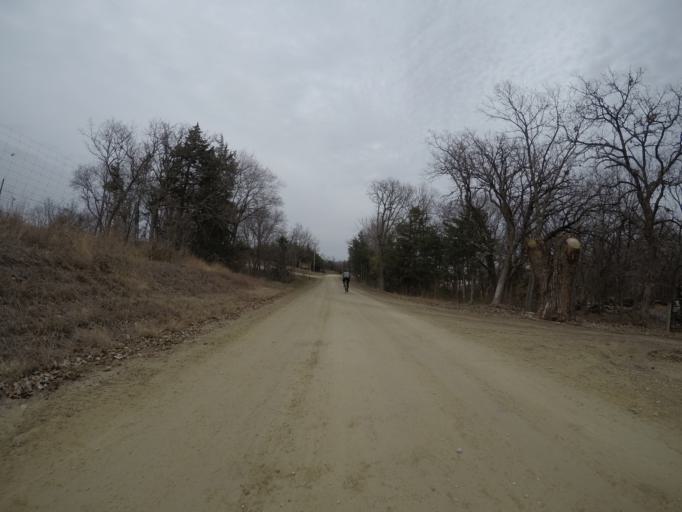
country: US
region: Kansas
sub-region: Riley County
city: Ogden
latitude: 39.1902
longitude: -96.6751
